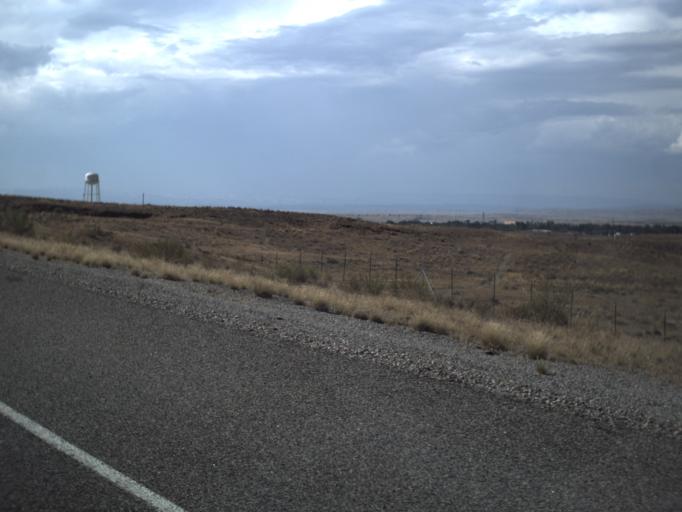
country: US
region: Utah
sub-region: Carbon County
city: East Carbon City
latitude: 38.9764
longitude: -110.1260
